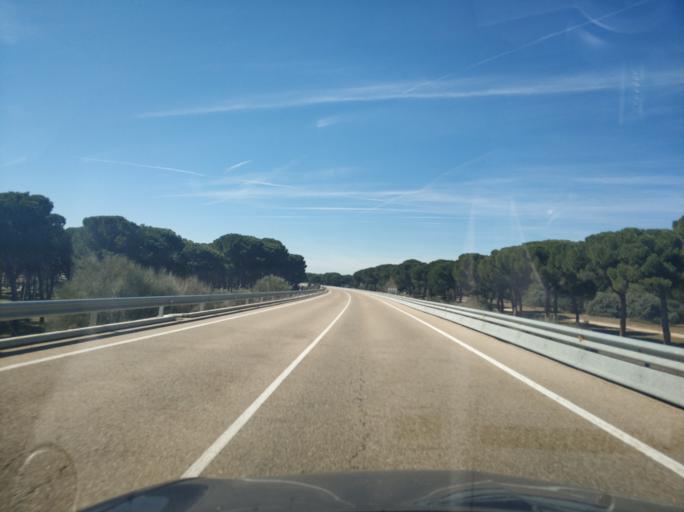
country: ES
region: Castille and Leon
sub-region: Provincia de Valladolid
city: Viana de Cega
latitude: 41.5335
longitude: -4.7380
